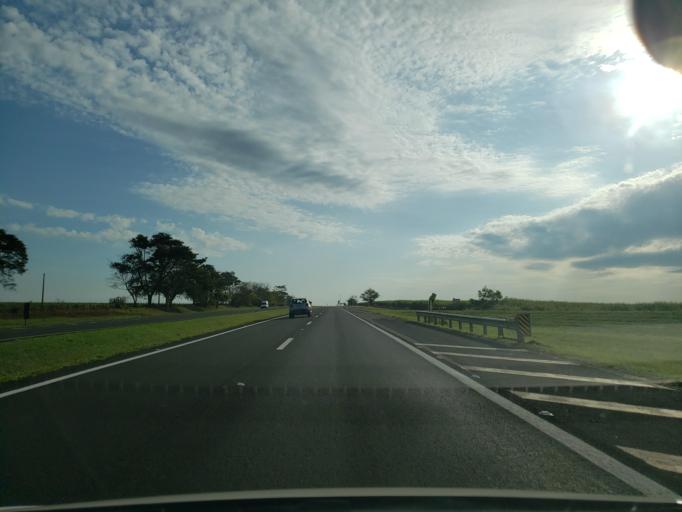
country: BR
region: Sao Paulo
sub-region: Valparaiso
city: Valparaiso
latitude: -21.2049
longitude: -50.7958
